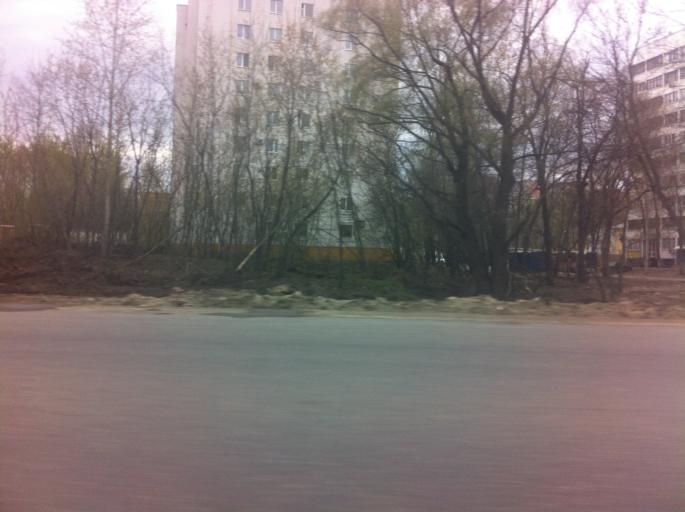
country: RU
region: Samara
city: Volzhskiy
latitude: 53.3511
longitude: 50.2166
